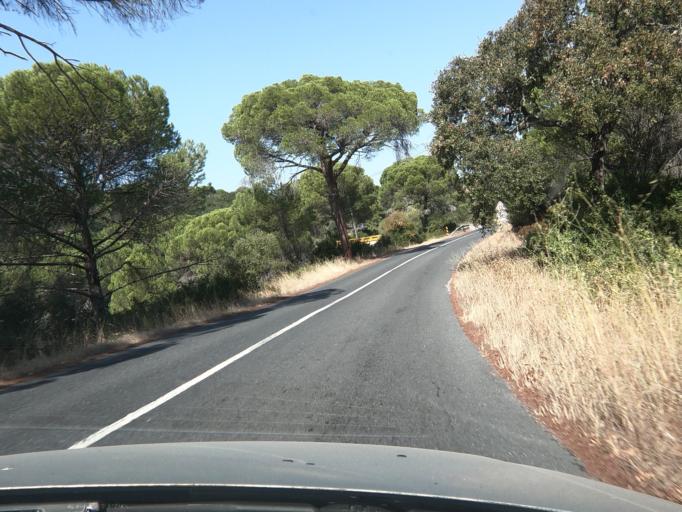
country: PT
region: Setubal
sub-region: Alcacer do Sal
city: Alcacer do Sal
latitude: 38.3097
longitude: -8.4312
